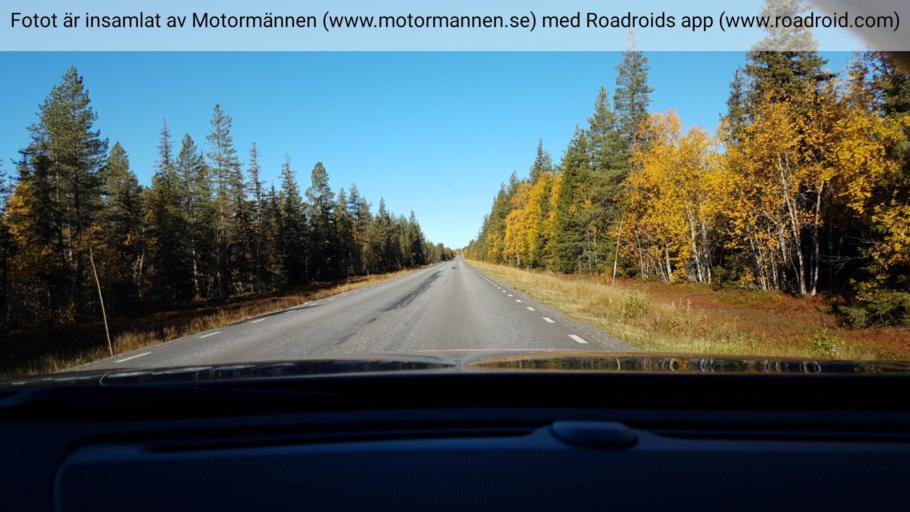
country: SE
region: Vaesterbotten
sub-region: Skelleftea Kommun
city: Storvik
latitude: 65.3560
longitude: 20.4668
